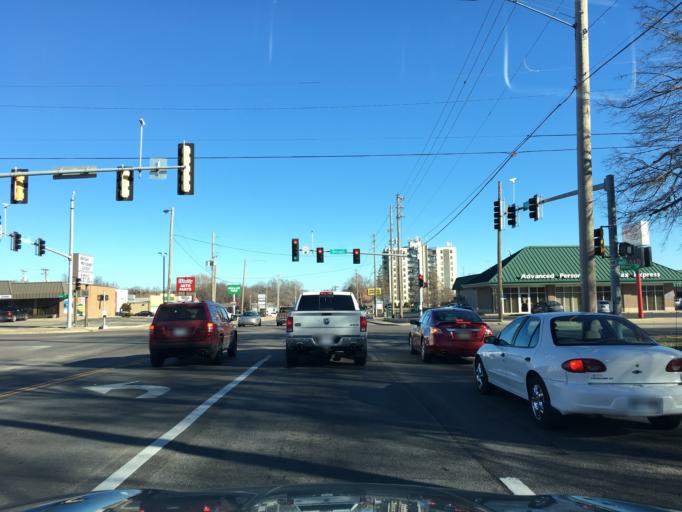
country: US
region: Kansas
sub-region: Sedgwick County
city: Wichita
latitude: 37.6719
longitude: -97.2810
